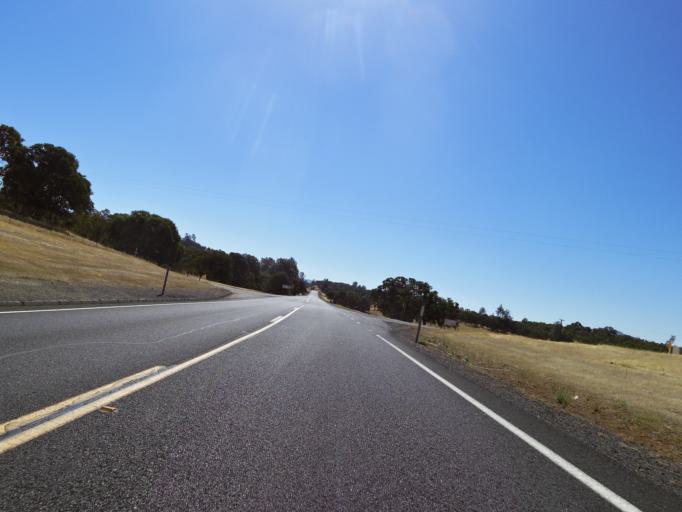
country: US
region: California
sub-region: Tuolumne County
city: Tuolumne City
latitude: 37.7013
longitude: -120.2962
